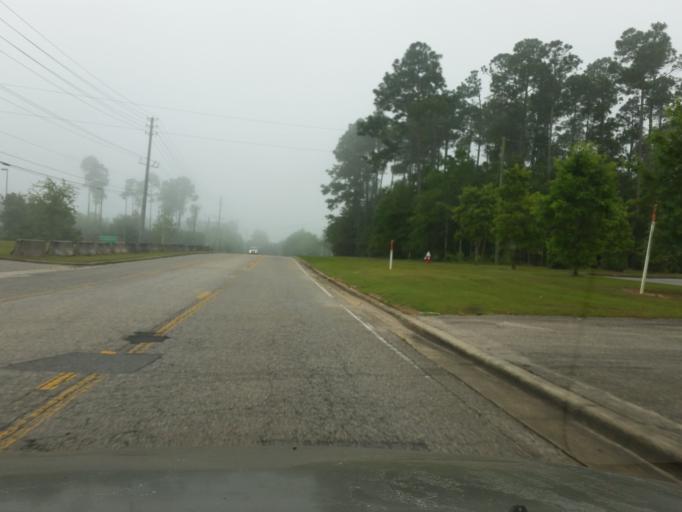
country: US
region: Florida
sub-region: Escambia County
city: Ferry Pass
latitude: 30.5221
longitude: -87.1900
